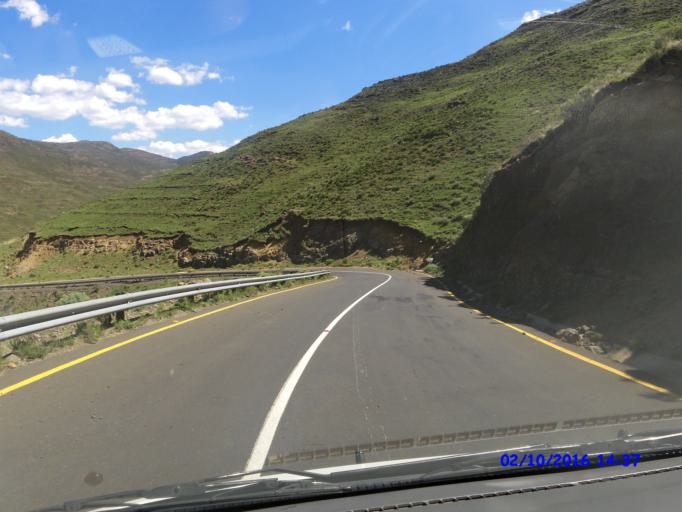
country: LS
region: Maseru
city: Nako
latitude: -29.5020
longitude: 28.0626
